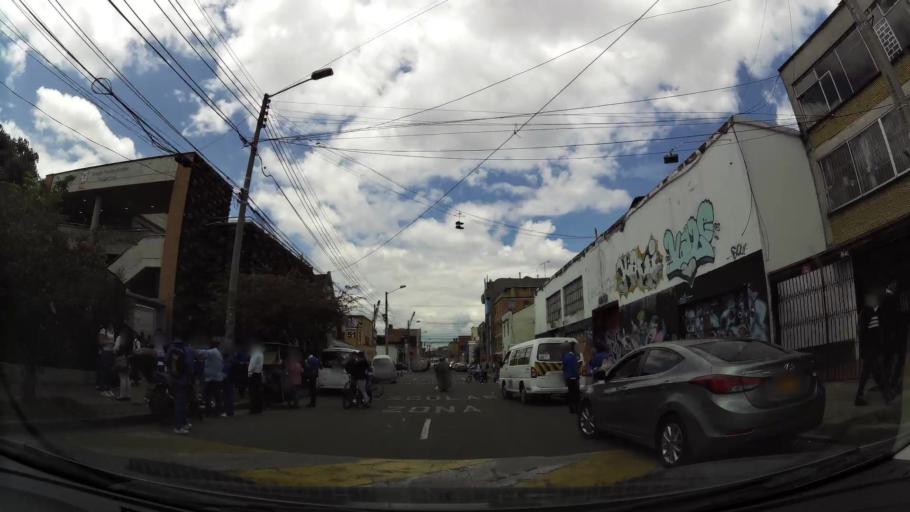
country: CO
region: Bogota D.C.
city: Bogota
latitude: 4.6381
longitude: -74.0739
